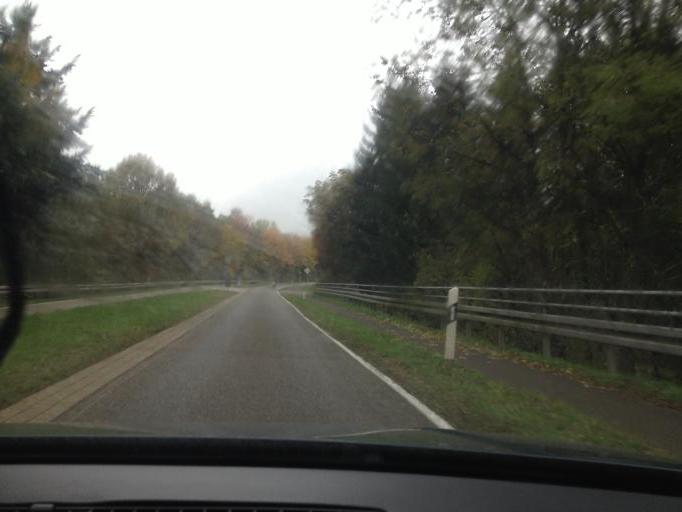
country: DE
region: Saarland
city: Tholey
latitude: 49.4666
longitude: 7.0039
